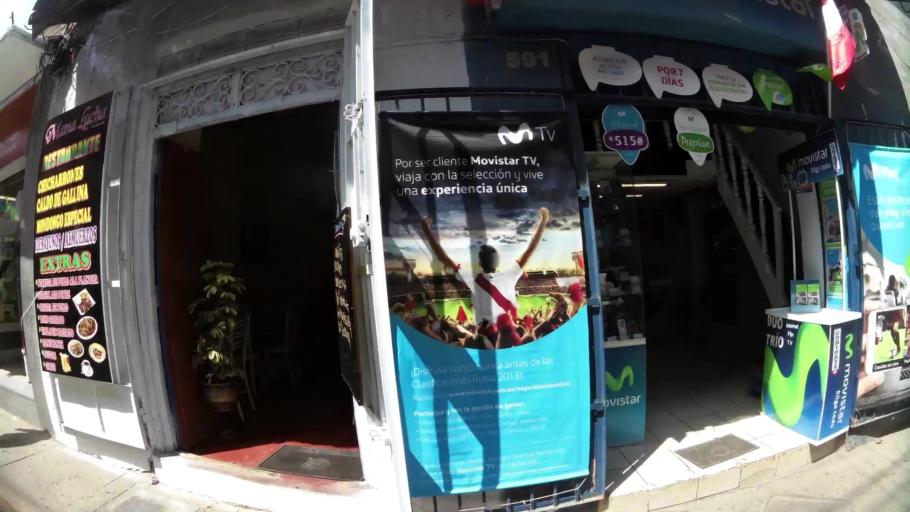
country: PE
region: Junin
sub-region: Provincia de Huancayo
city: Huancayo
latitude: -12.0713
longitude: -75.2094
